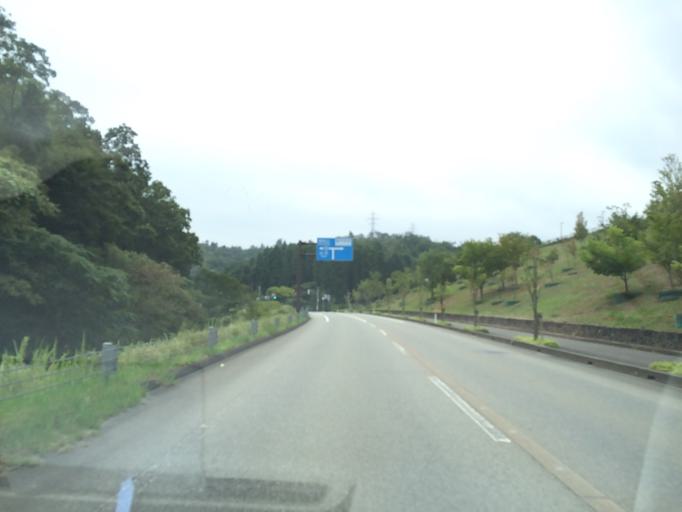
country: JP
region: Hyogo
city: Toyooka
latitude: 35.5278
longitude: 134.8087
